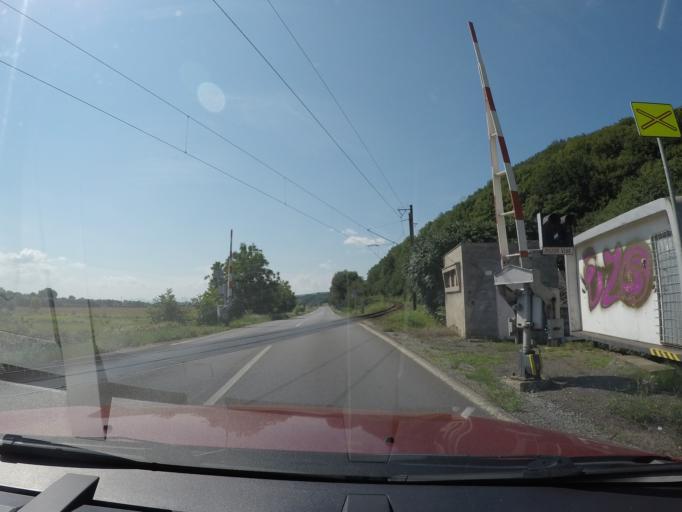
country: SK
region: Presovsky
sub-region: Okres Presov
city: Presov
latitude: 48.8970
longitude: 21.2437
